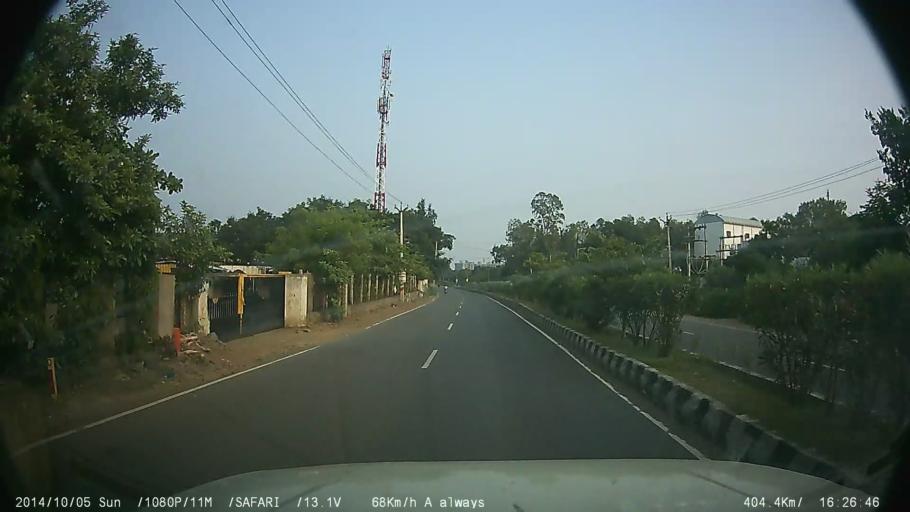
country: IN
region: Tamil Nadu
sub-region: Kancheepuram
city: Vengavasal
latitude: 12.8050
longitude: 80.1906
